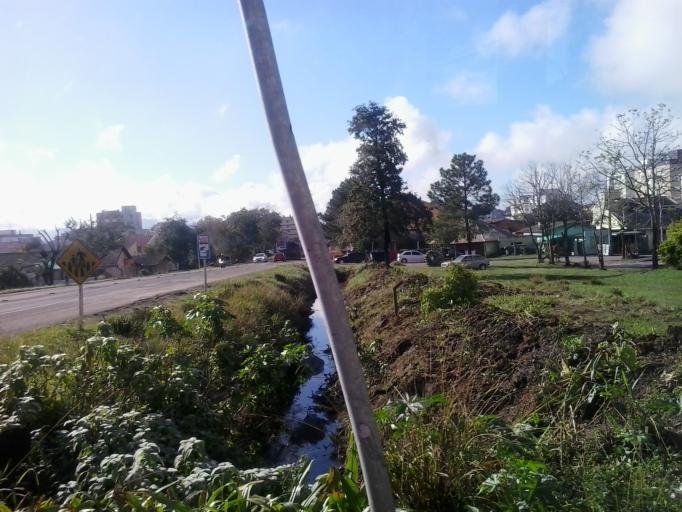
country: BR
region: Rio Grande do Sul
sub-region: Santa Maria
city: Santa Maria
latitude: -29.7055
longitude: -53.7253
